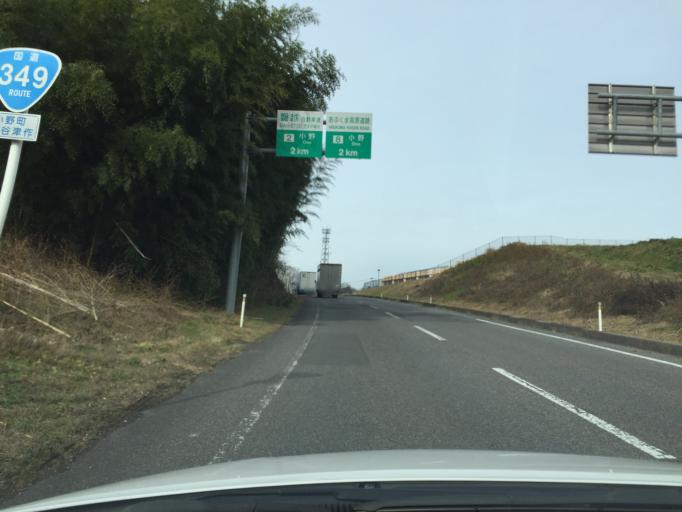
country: JP
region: Fukushima
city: Funehikimachi-funehiki
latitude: 37.2743
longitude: 140.6280
